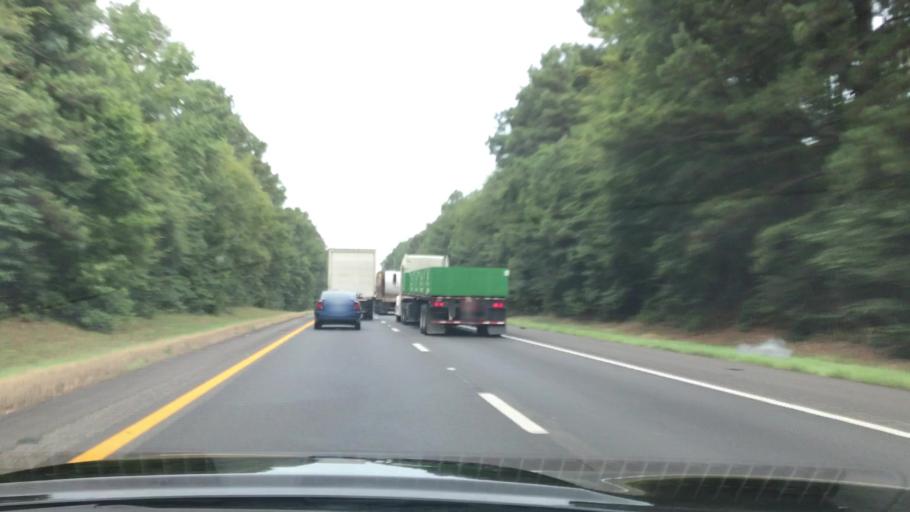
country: US
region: Texas
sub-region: Harrison County
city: Marshall
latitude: 32.4879
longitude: -94.4471
